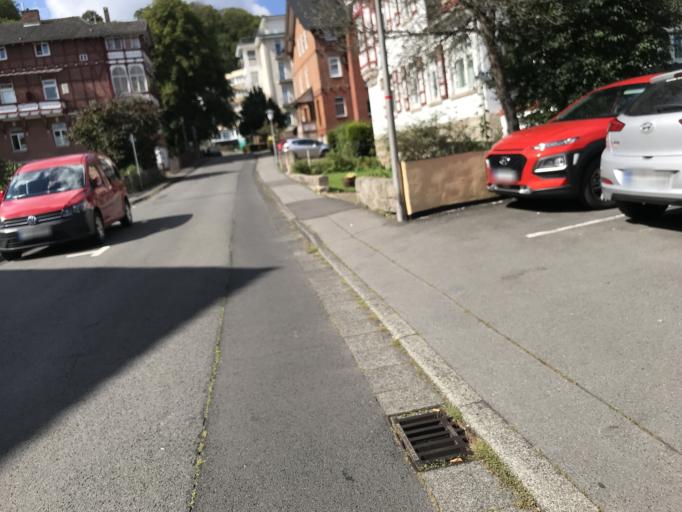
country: DE
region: Hesse
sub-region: Regierungsbezirk Kassel
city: Bad Sooden-Allendorf
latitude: 51.2698
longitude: 9.9631
